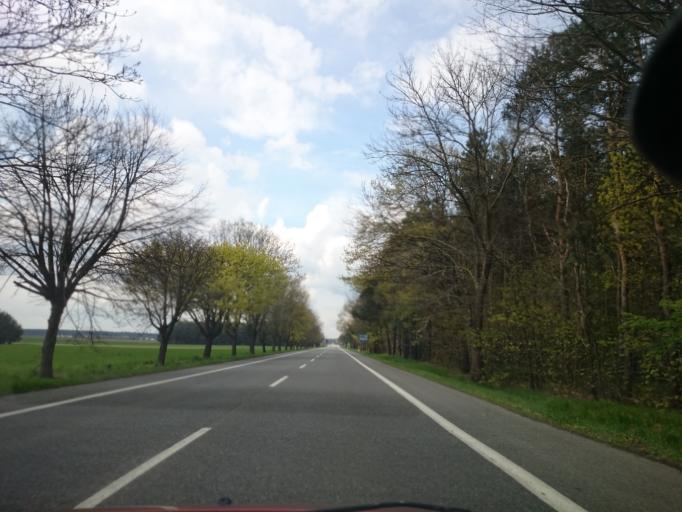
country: PL
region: Opole Voivodeship
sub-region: Powiat strzelecki
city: Izbicko
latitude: 50.5748
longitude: 18.1406
